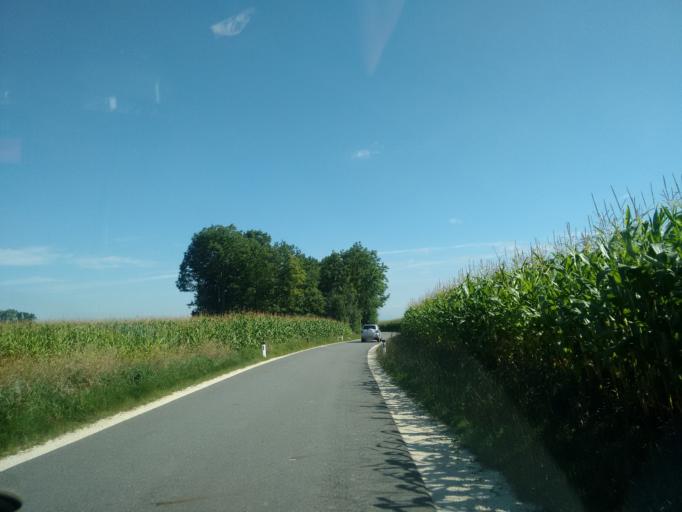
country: AT
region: Upper Austria
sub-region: Politischer Bezirk Steyr-Land
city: Pfarrkirchen bei Bad Hall
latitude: 48.0002
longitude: 14.1600
